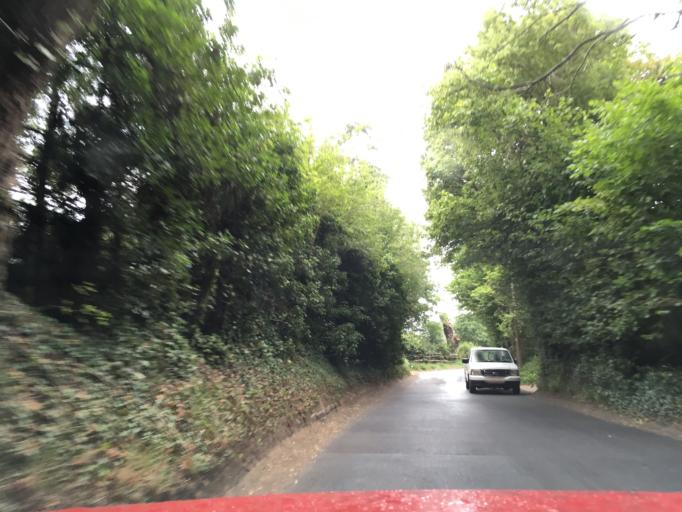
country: GB
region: England
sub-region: Kent
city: Yalding
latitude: 51.2198
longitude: 0.4754
